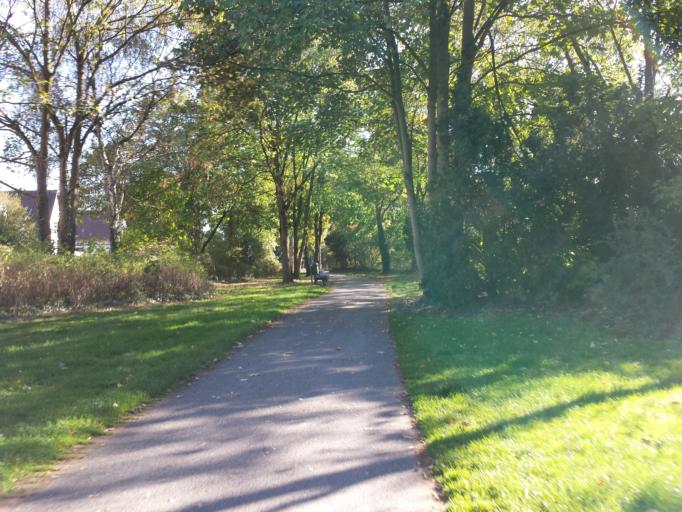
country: DE
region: Lower Saxony
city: Ritterhude
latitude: 53.1316
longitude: 8.7423
